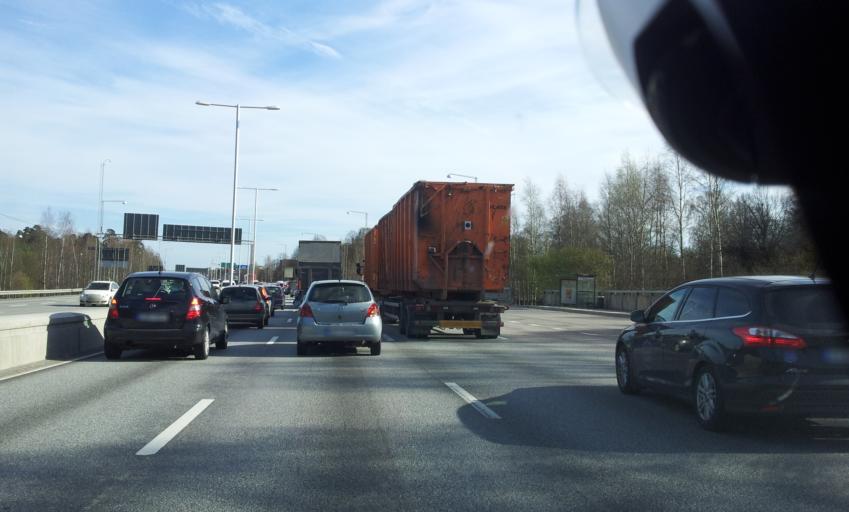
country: SE
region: Stockholm
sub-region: Norrtalje Kommun
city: Bergshamra
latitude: 59.3595
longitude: 18.0281
